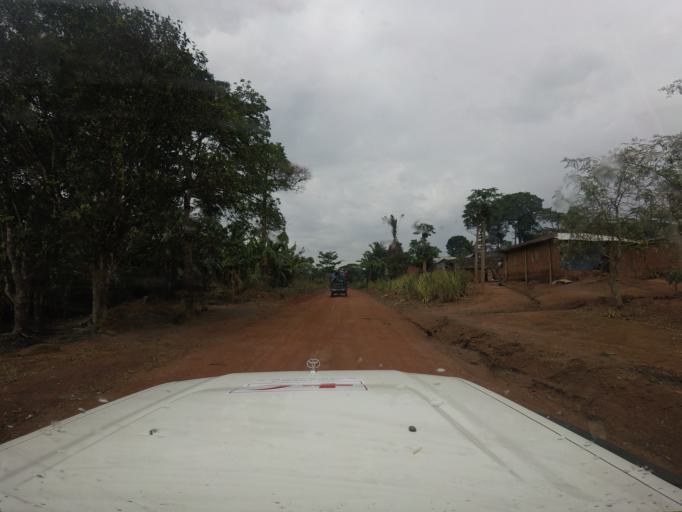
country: SL
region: Eastern Province
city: Buedu
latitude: 8.3165
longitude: -10.1516
